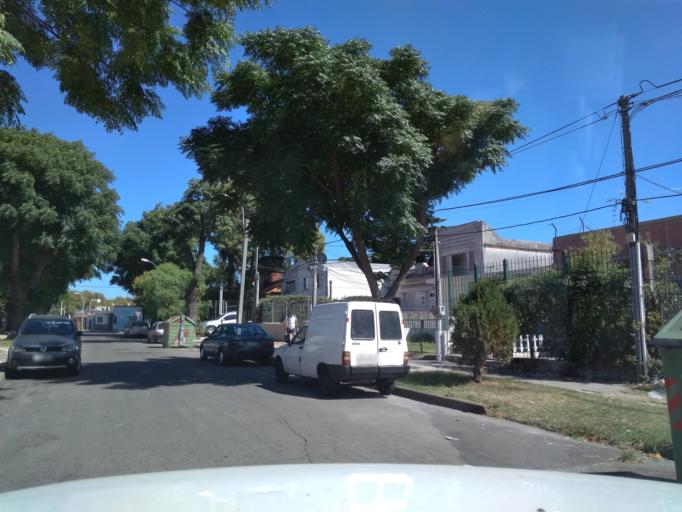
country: UY
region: Montevideo
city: Montevideo
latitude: -34.8857
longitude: -56.1278
